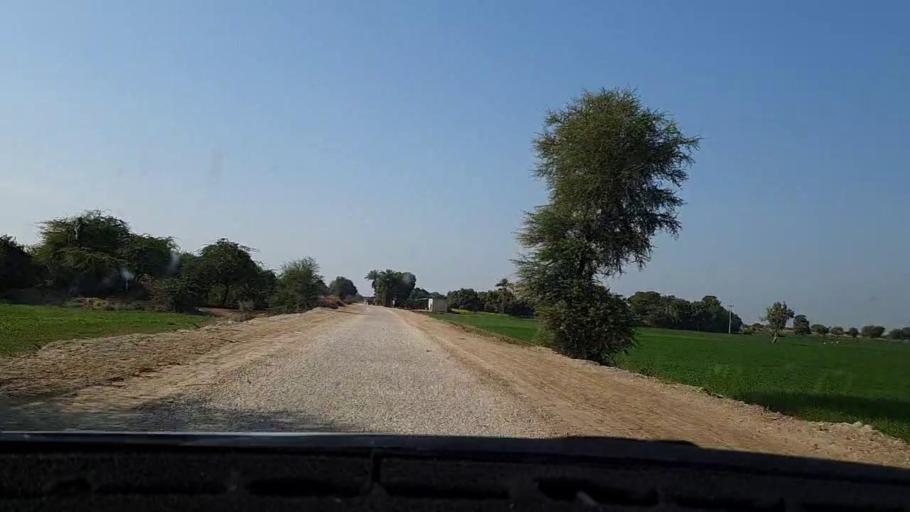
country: PK
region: Sindh
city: Tando Mittha Khan
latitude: 25.8135
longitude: 69.3112
